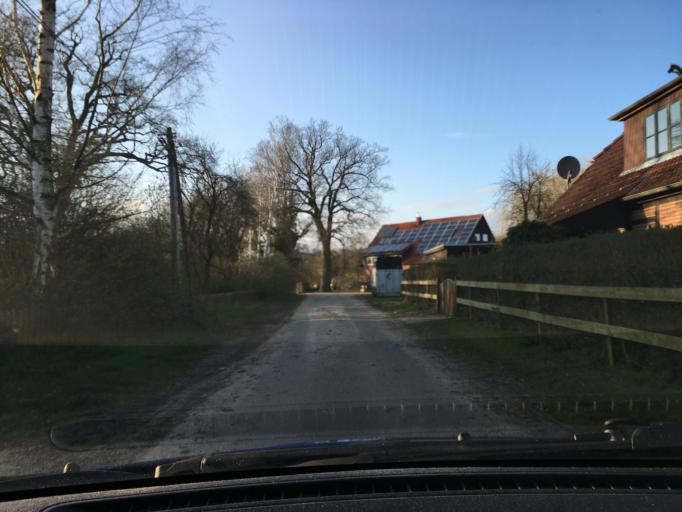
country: DE
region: Lower Saxony
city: Hittbergen
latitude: 53.3279
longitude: 10.6242
